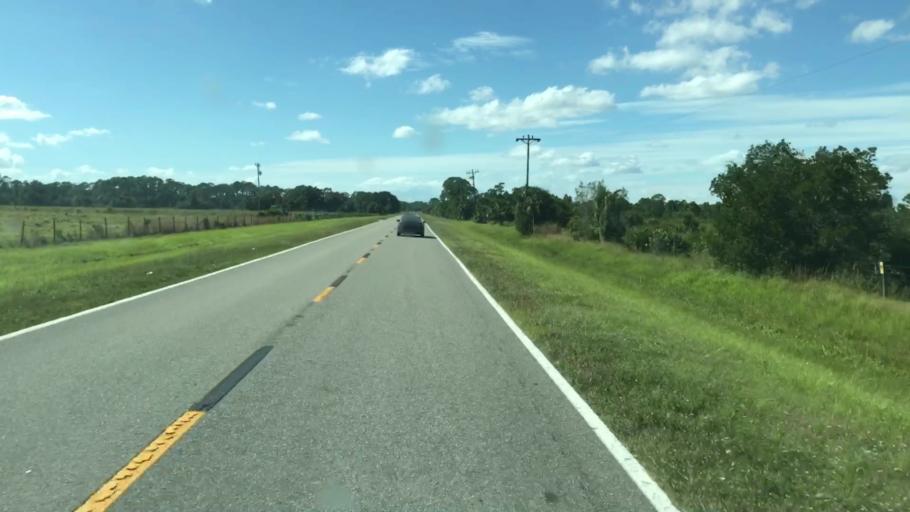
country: US
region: Florida
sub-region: Lee County
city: Fort Myers Shores
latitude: 26.7401
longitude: -81.7474
